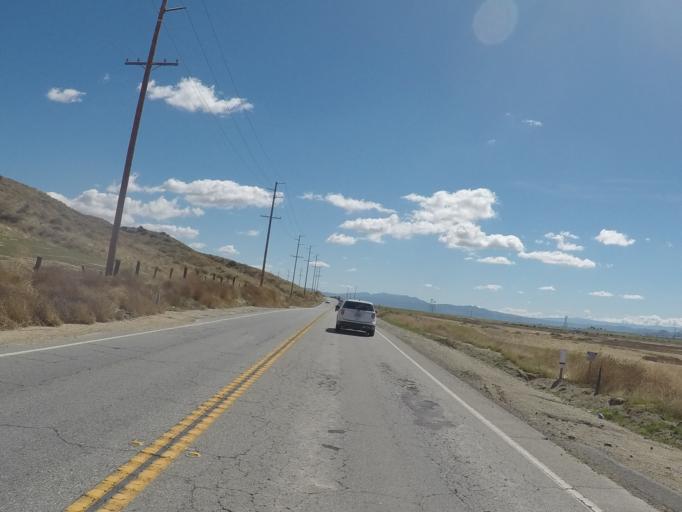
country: US
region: California
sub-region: Riverside County
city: Lakeview
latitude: 33.8742
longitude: -117.0501
